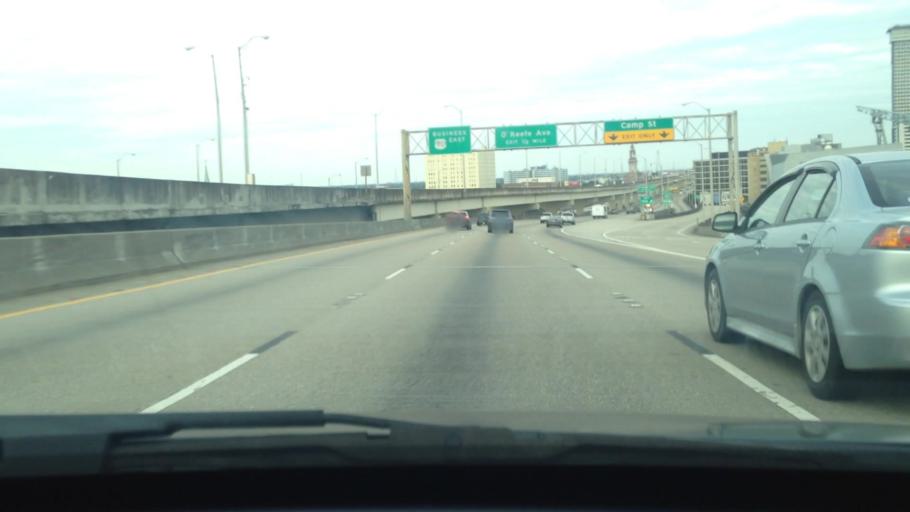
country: US
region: Louisiana
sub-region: Orleans Parish
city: New Orleans
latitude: 29.9396
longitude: -90.0677
